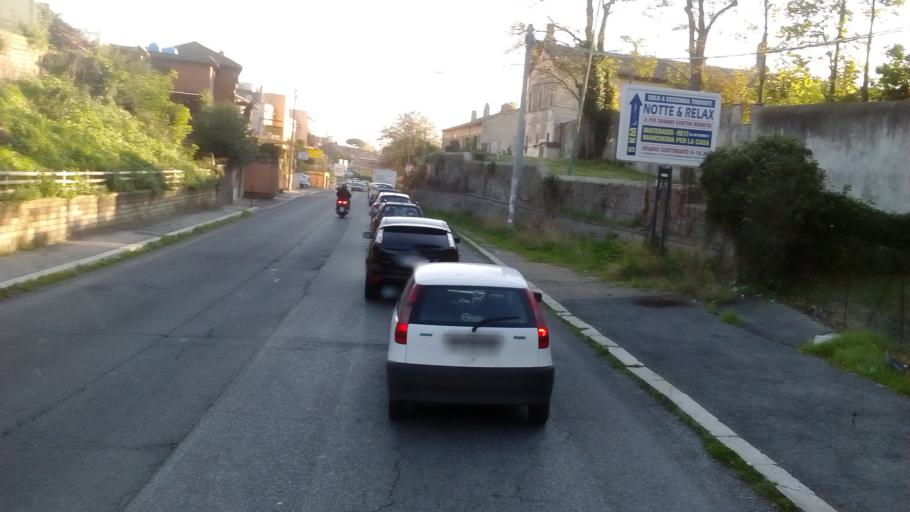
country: IT
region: Latium
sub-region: Citta metropolitana di Roma Capitale
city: Pavona
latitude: 41.7311
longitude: 12.6163
